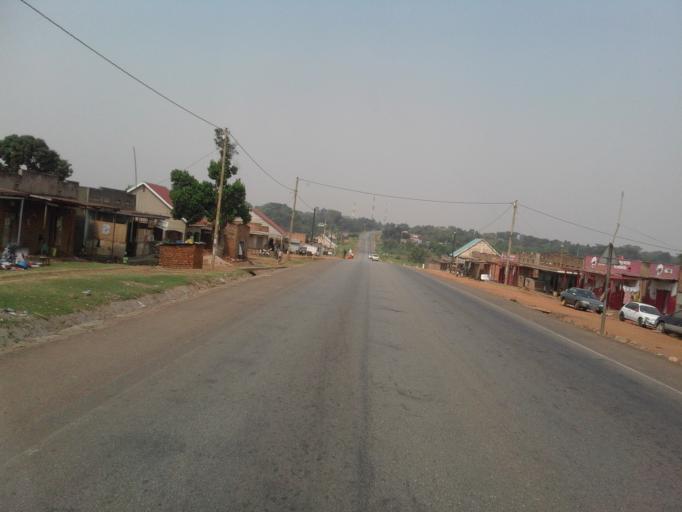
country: UG
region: Eastern Region
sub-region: Bugiri District
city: Bugiri
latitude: 0.6235
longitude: 33.6195
